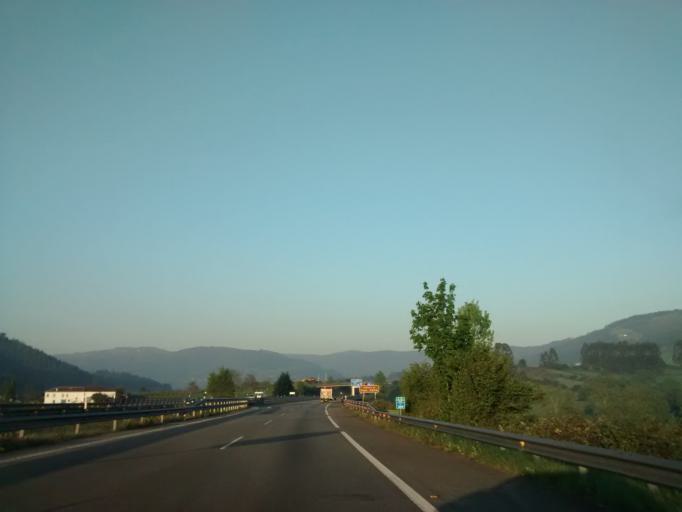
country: ES
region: Asturias
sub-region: Province of Asturias
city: Villaviciosa
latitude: 43.4717
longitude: -5.4690
